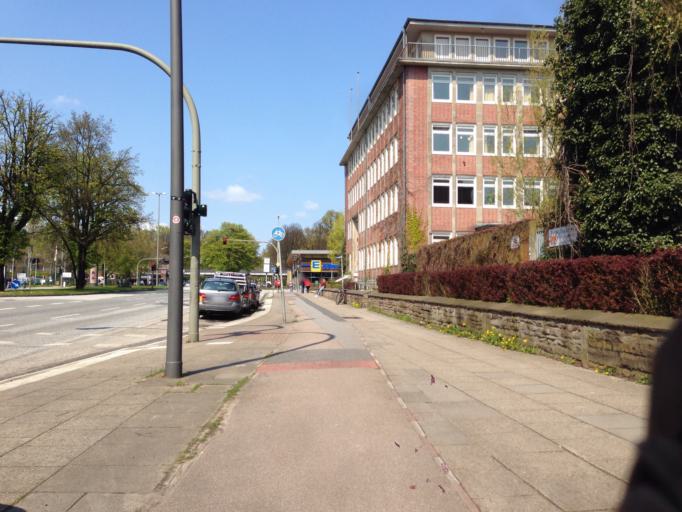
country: DE
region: Hamburg
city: Barmbek-Nord
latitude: 53.5870
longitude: 10.0337
